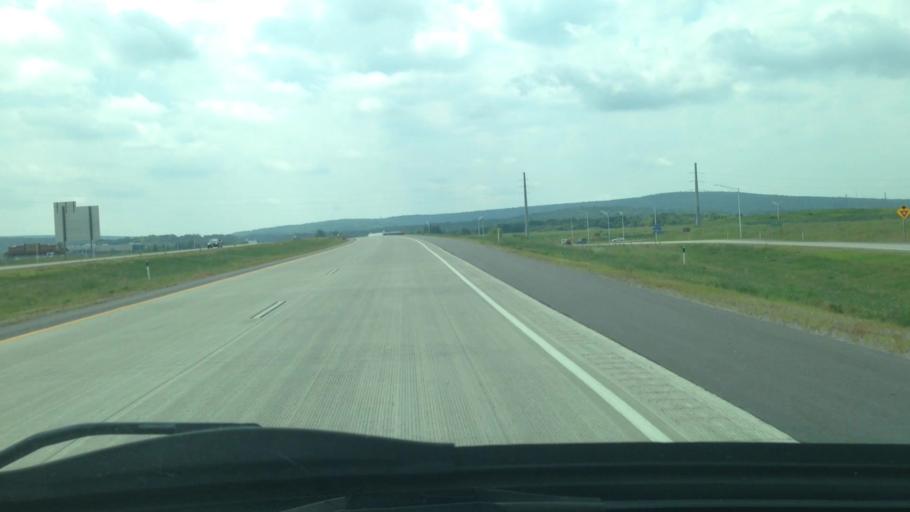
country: US
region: Wisconsin
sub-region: Sauk County
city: West Baraboo
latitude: 43.4630
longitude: -89.7778
